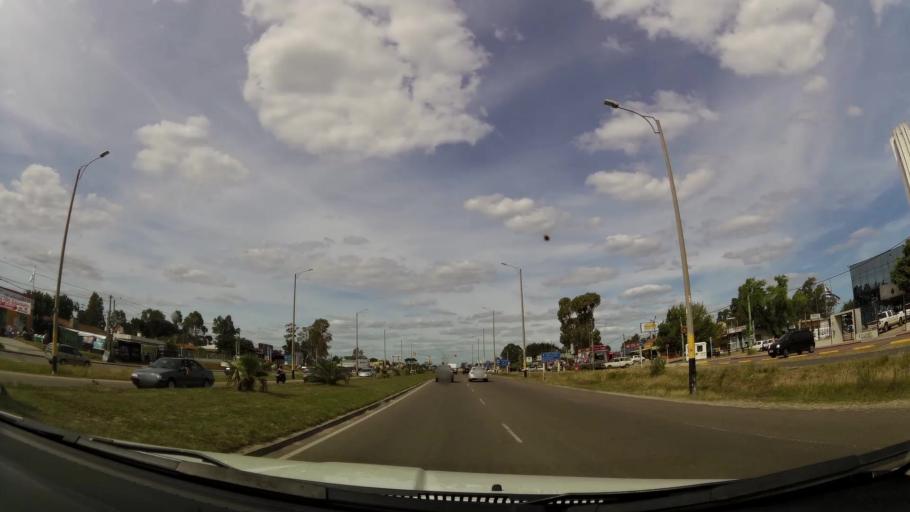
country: UY
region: Canelones
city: Barra de Carrasco
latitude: -34.8328
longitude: -55.9782
